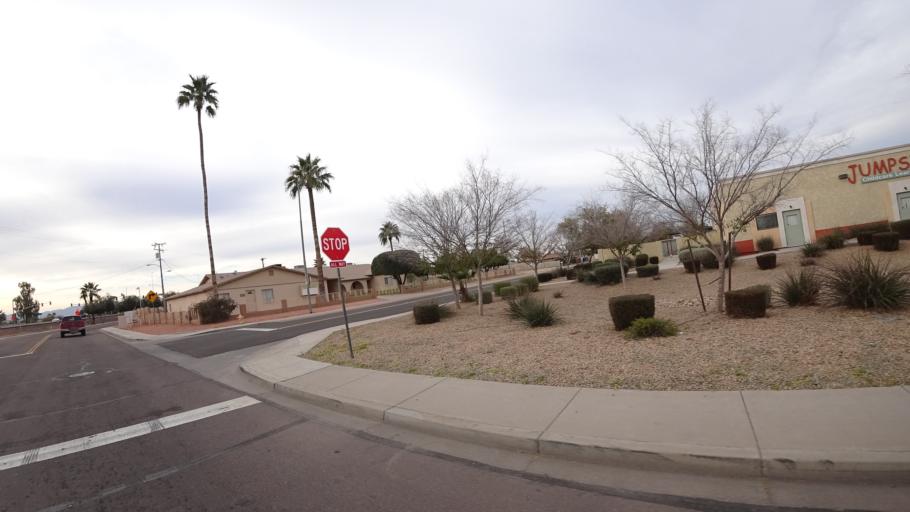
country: US
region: Arizona
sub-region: Maricopa County
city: Surprise
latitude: 33.6235
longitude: -112.3289
